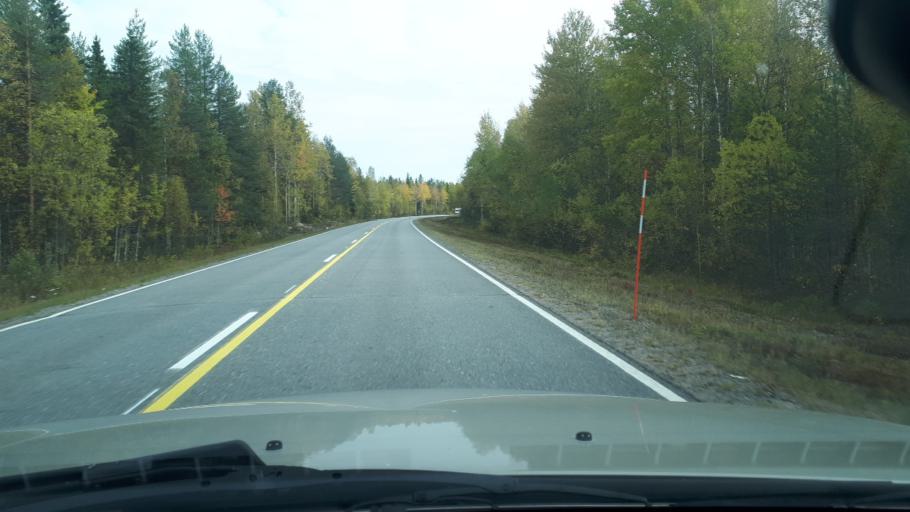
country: FI
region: Lapland
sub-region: Rovaniemi
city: Ranua
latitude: 66.0080
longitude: 26.2778
